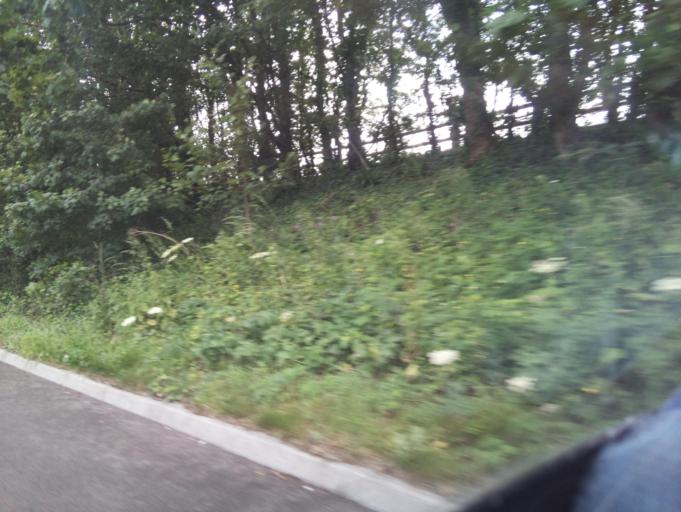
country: GB
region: Wales
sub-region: Vale of Glamorgan
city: Llantwit Major
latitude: 51.4064
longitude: -3.4582
